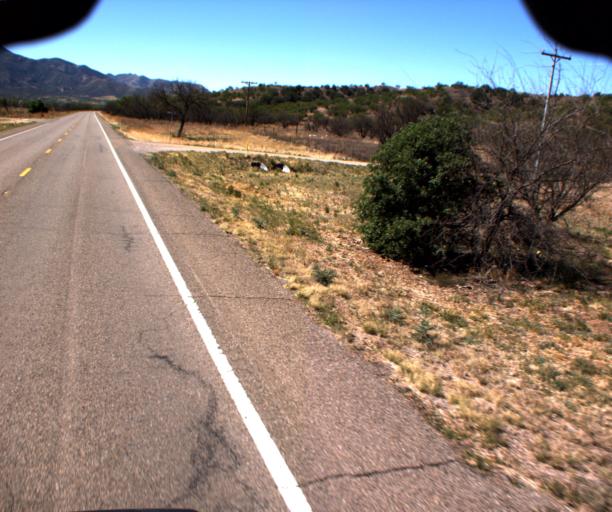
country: US
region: Arizona
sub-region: Santa Cruz County
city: Rio Rico
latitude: 31.5745
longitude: -110.7295
